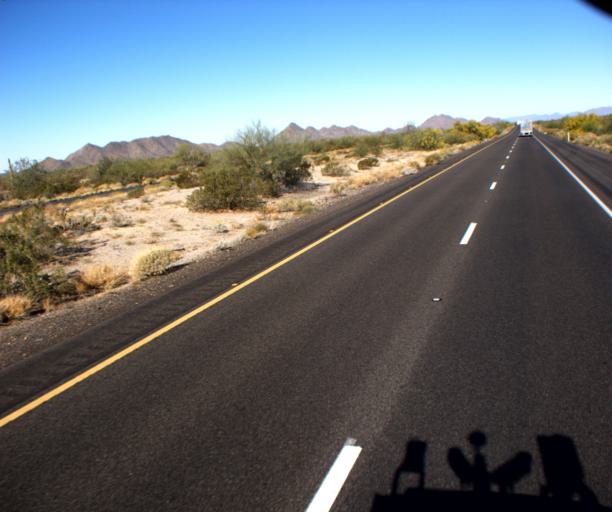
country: US
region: Arizona
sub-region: Maricopa County
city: Gila Bend
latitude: 32.8819
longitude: -112.4596
